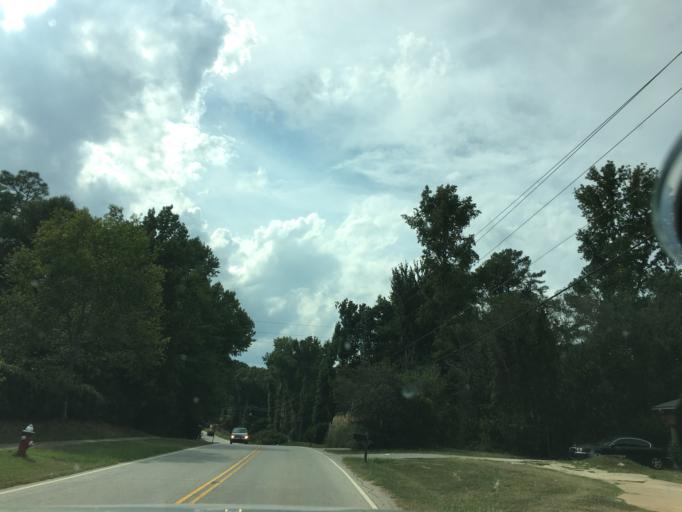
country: US
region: South Carolina
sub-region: Lexington County
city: Irmo
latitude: 34.0681
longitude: -81.1870
